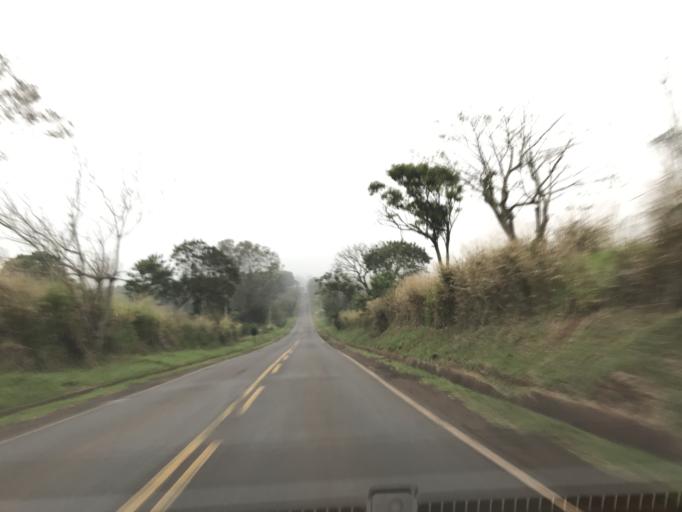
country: PY
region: Canindeyu
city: Salto del Guaira
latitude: -24.1007
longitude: -54.1024
